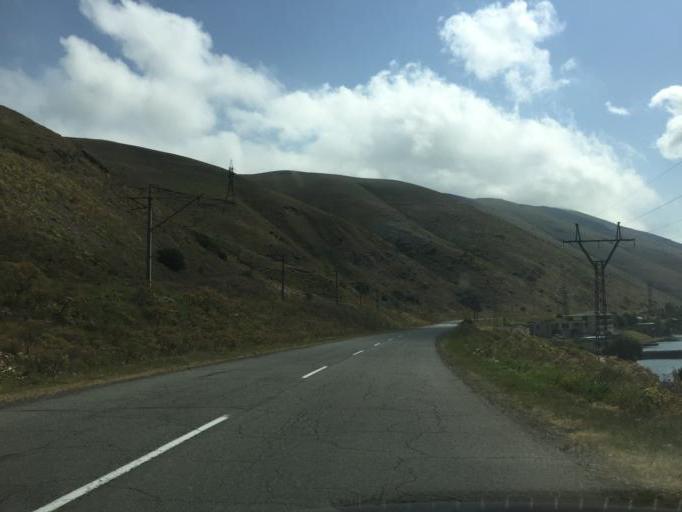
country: AM
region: Geghark'unik'i Marz
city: Tsovagyugh
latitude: 40.6319
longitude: 44.9823
